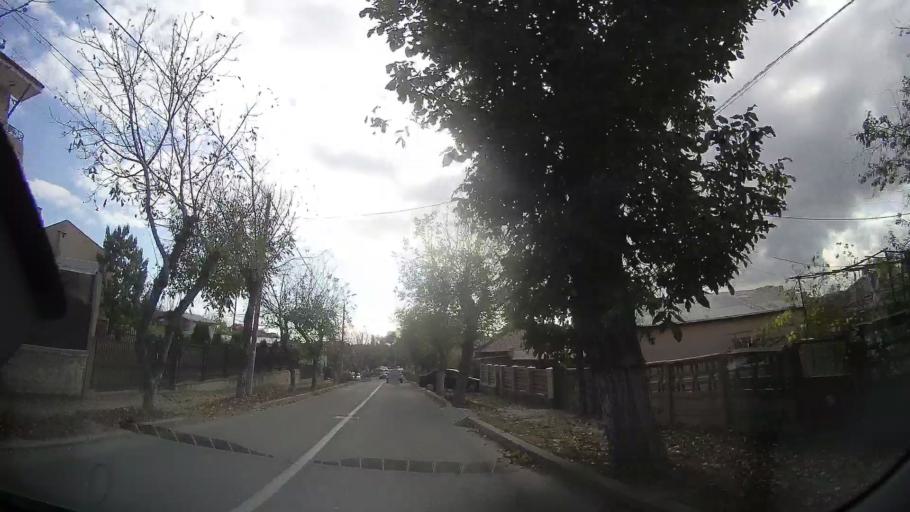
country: RO
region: Constanta
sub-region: Oras Techirghiol
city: Techirghiol
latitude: 44.0570
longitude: 28.6003
